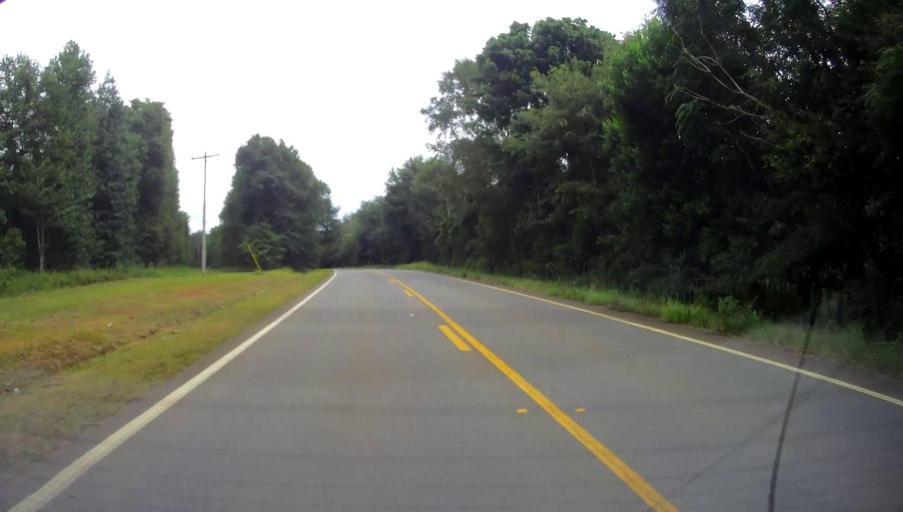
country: US
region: Georgia
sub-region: Schley County
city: Ellaville
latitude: 32.2502
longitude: -84.3850
